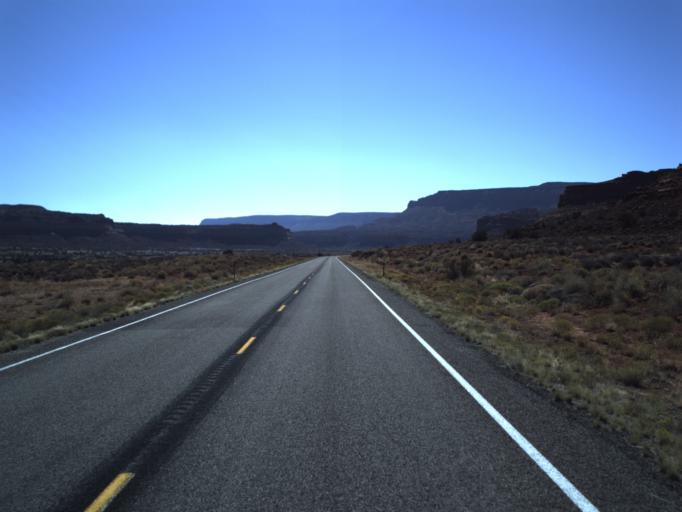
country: US
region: Utah
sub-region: San Juan County
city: Blanding
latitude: 37.7804
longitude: -110.2918
